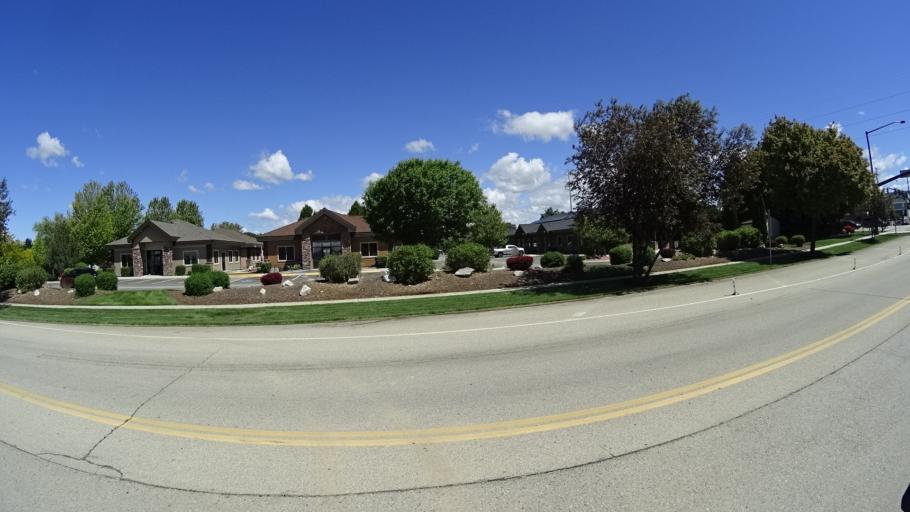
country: US
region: Idaho
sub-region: Ada County
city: Meridian
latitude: 43.6266
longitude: -116.3555
